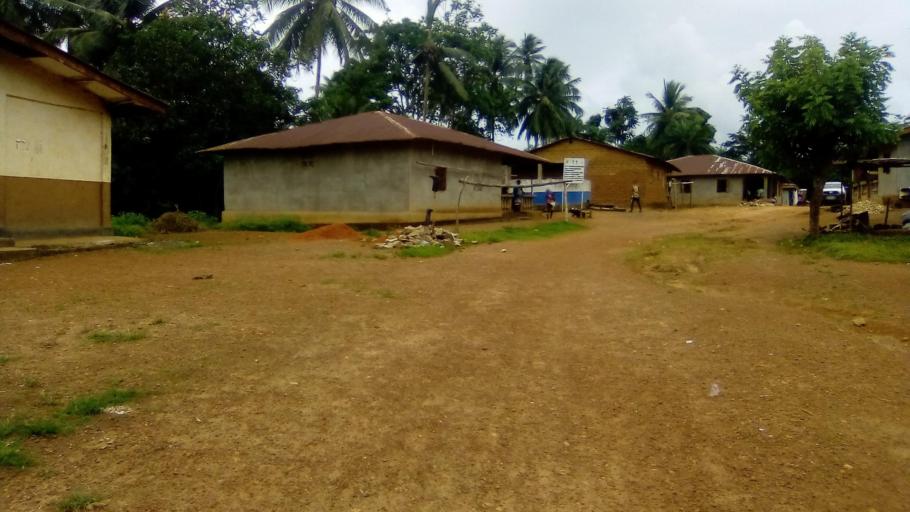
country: SL
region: Southern Province
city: Pujehun
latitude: 7.3722
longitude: -11.7099
